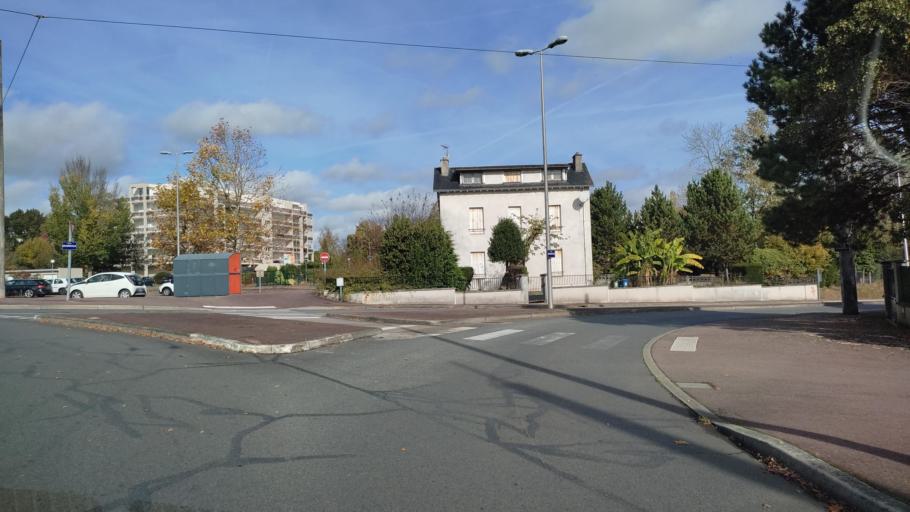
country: FR
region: Limousin
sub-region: Departement de la Haute-Vienne
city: Isle
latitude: 45.8135
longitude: 1.2286
